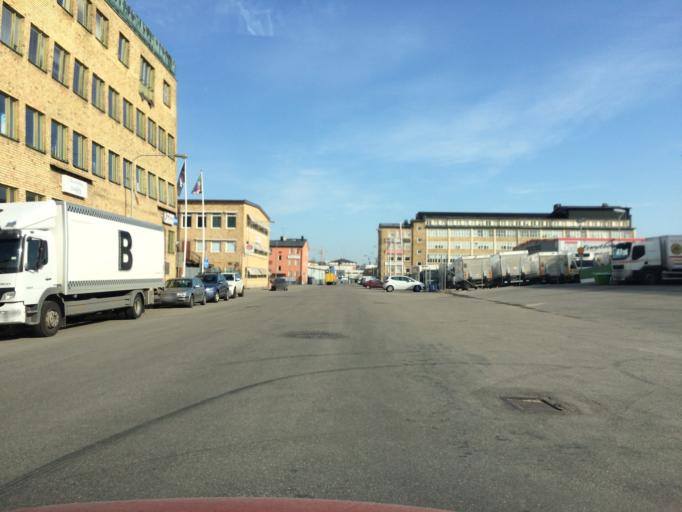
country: SE
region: Stockholm
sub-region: Stockholms Kommun
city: Arsta
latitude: 59.2968
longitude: 18.0153
